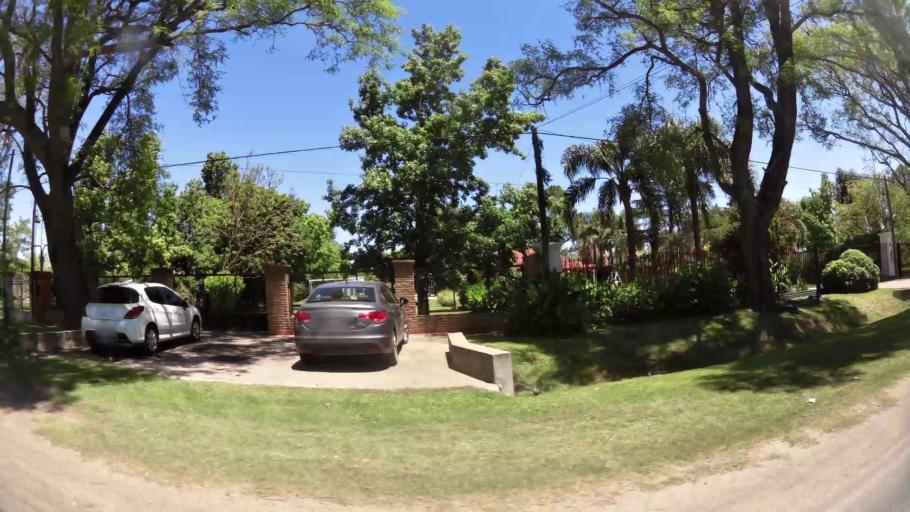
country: AR
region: Santa Fe
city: Bella Italia
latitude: -31.2669
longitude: -61.4347
